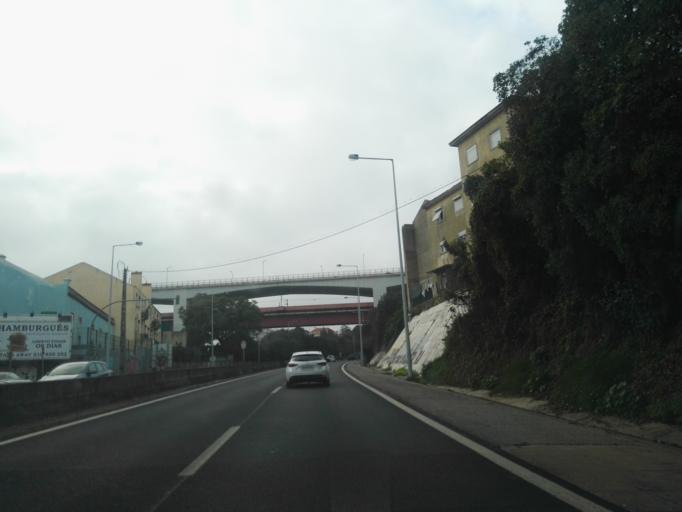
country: PT
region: Setubal
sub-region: Almada
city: Pragal
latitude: 38.7070
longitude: -9.1759
